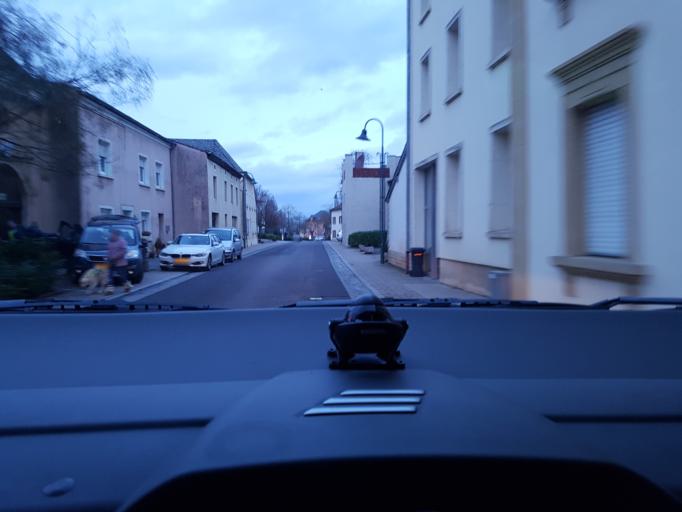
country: LU
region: Grevenmacher
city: Schengen
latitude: 49.4902
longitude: 6.3514
